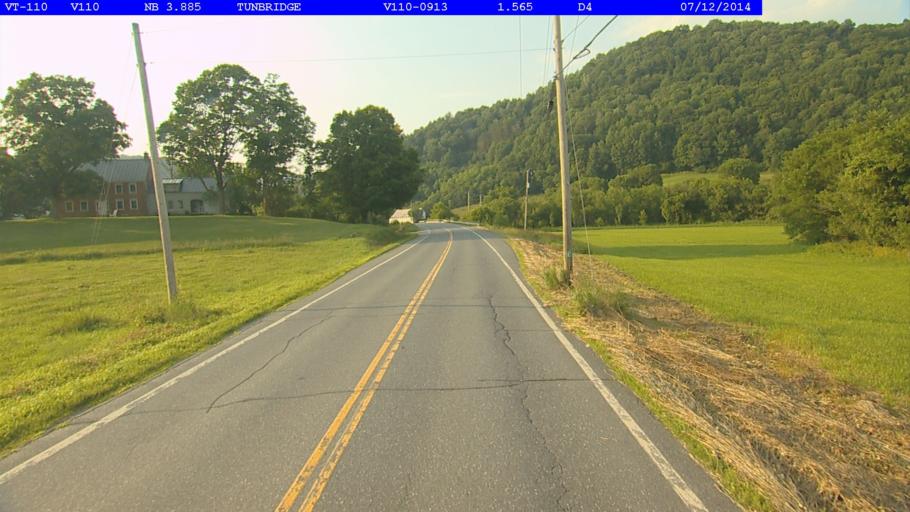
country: US
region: Vermont
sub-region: Orange County
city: Chelsea
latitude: 43.8733
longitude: -72.4987
